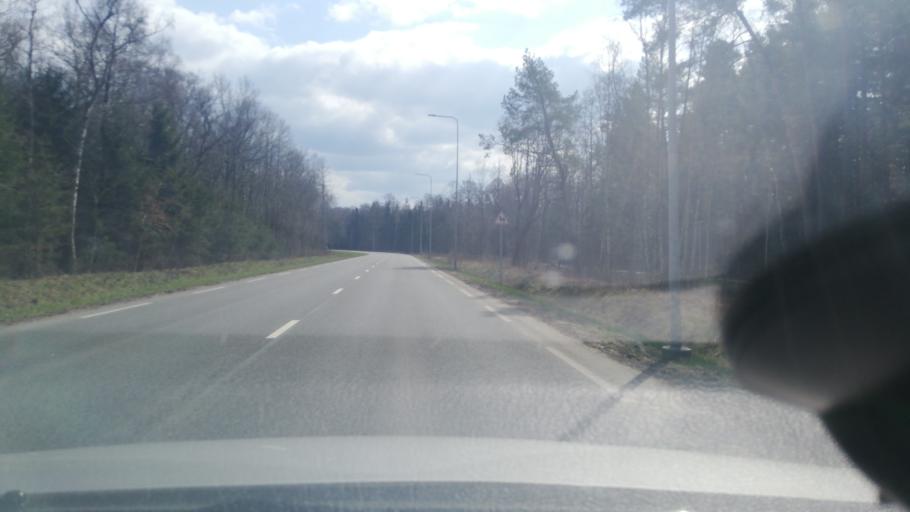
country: LT
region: Klaipedos apskritis
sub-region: Klaipeda
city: Klaipeda
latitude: 55.7563
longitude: 21.0894
